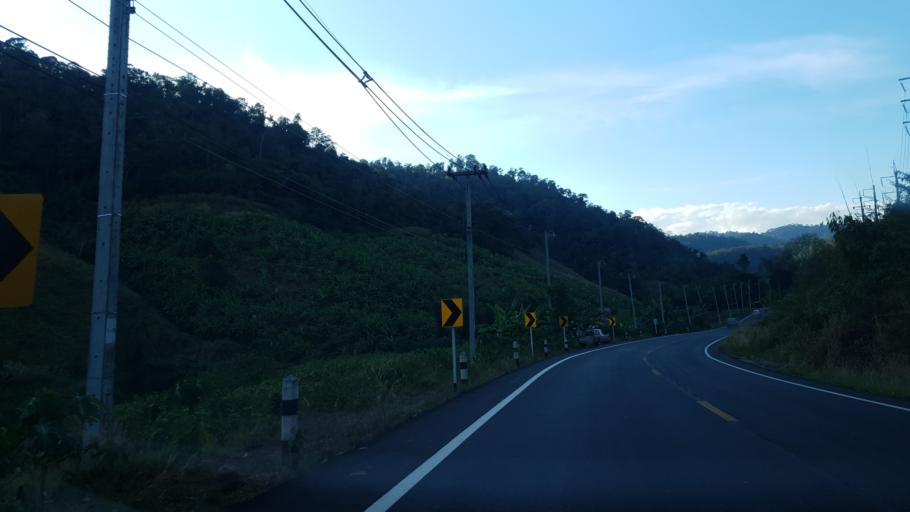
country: TH
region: Loei
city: Dan Sai
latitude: 17.2251
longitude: 101.0624
